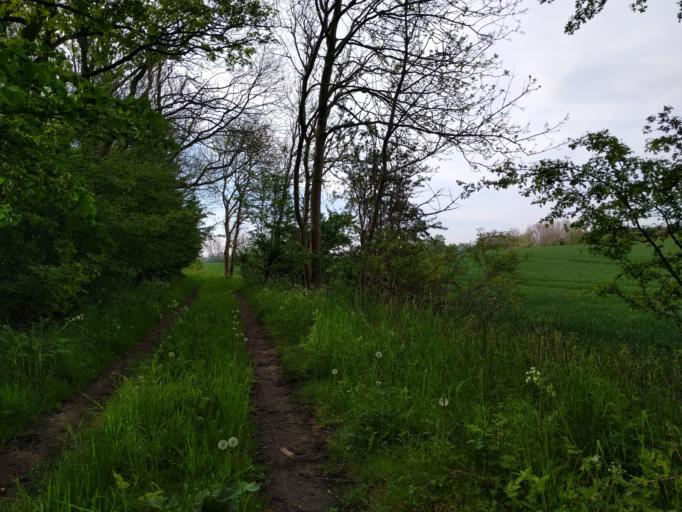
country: DK
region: South Denmark
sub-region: Odense Kommune
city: Bullerup
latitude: 55.3915
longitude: 10.5016
